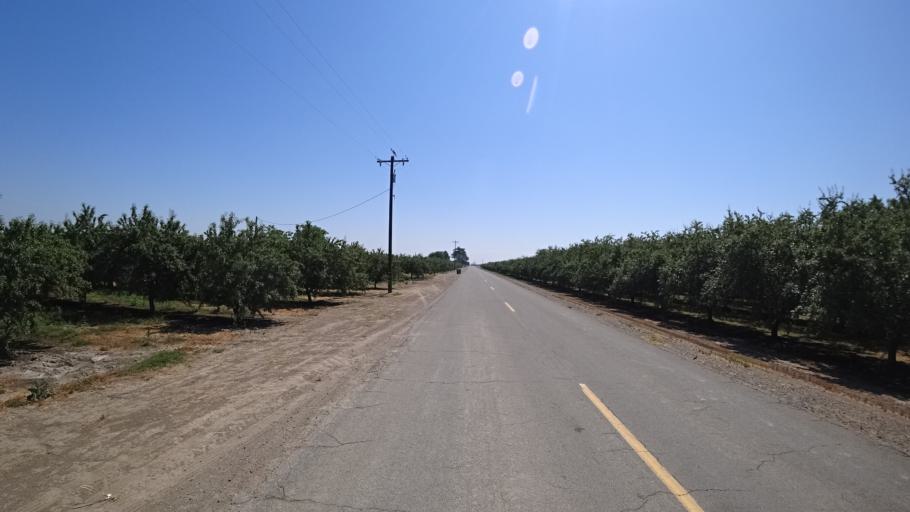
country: US
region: California
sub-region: Kings County
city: Armona
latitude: 36.3718
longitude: -119.7414
